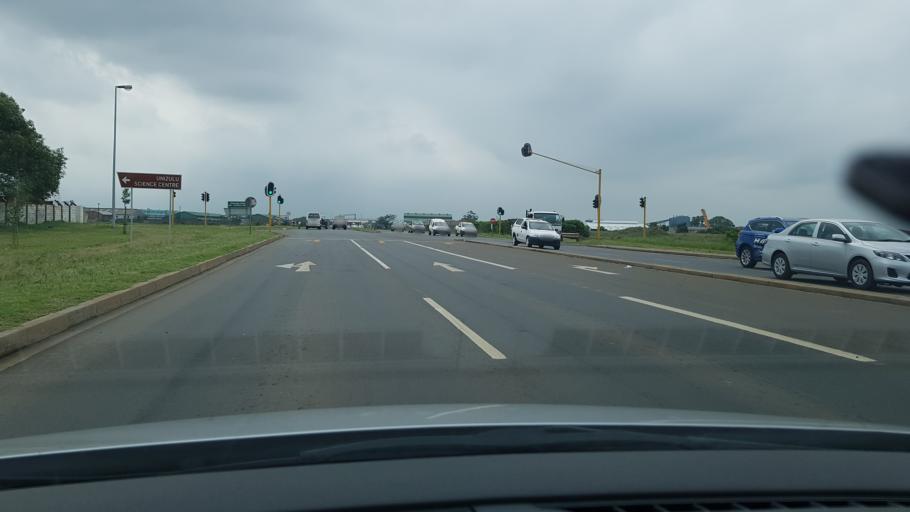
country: ZA
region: KwaZulu-Natal
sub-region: uThungulu District Municipality
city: Richards Bay
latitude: -28.7542
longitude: 32.0365
